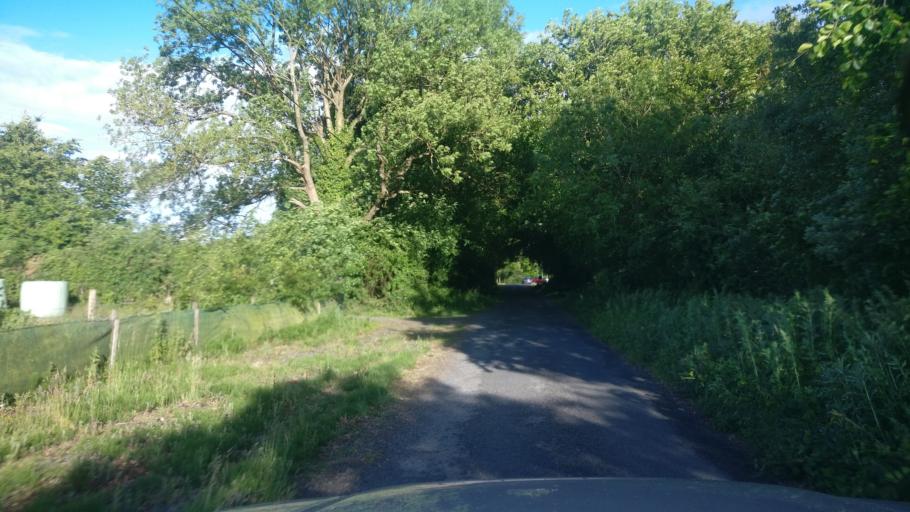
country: IE
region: Connaught
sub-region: County Galway
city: Ballinasloe
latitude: 53.2388
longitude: -8.1830
